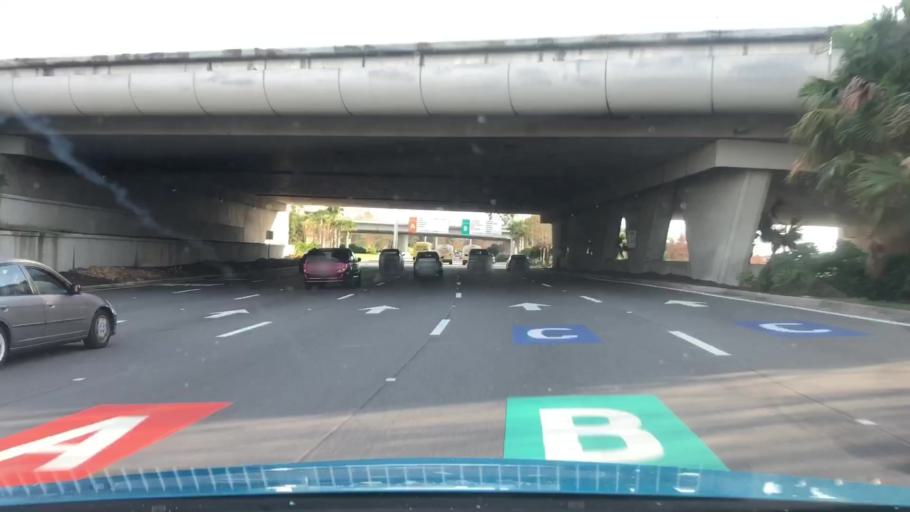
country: US
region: Florida
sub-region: Orange County
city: Belle Isle
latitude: 28.4399
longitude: -81.3116
